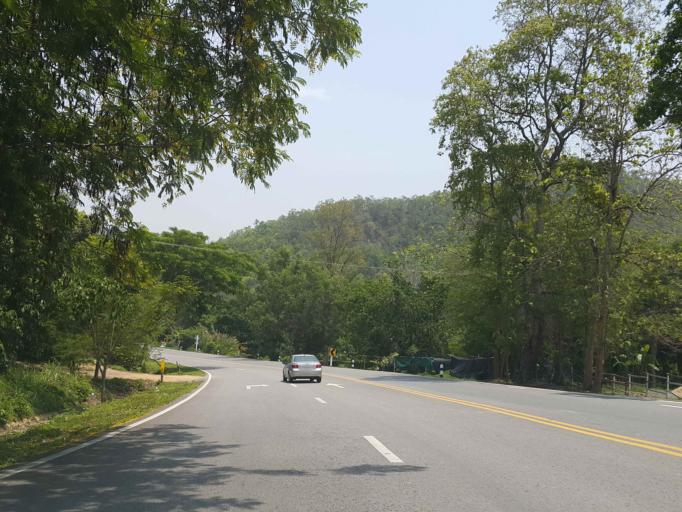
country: TH
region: Chiang Mai
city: Mae On
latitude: 18.9552
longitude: 99.2347
